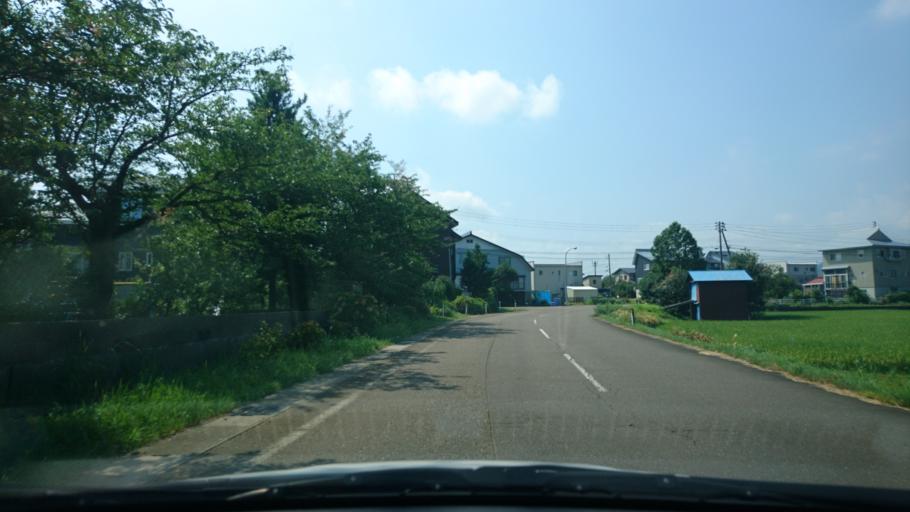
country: JP
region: Niigata
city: Arai
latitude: 37.0594
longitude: 138.2554
